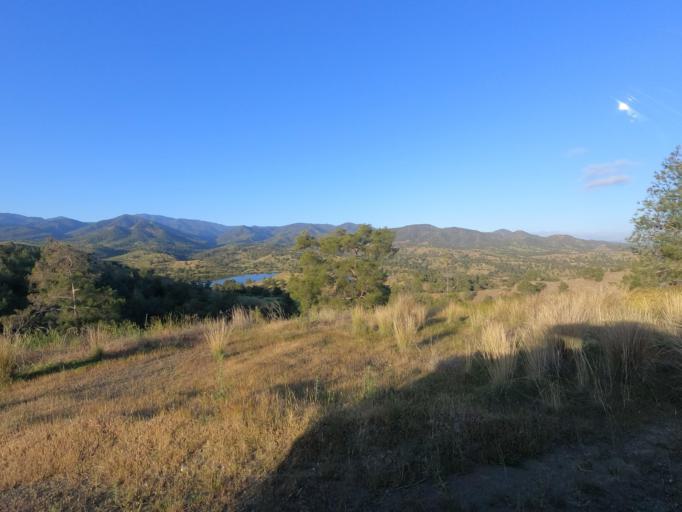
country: CY
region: Lefkosia
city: Astromeritis
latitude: 35.0667
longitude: 33.0337
